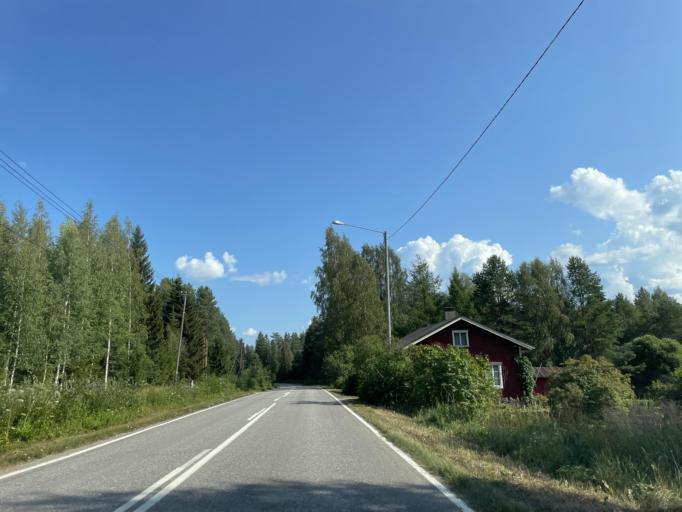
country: FI
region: Central Finland
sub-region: Saarijaervi-Viitasaari
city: Pihtipudas
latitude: 63.3566
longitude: 25.7559
